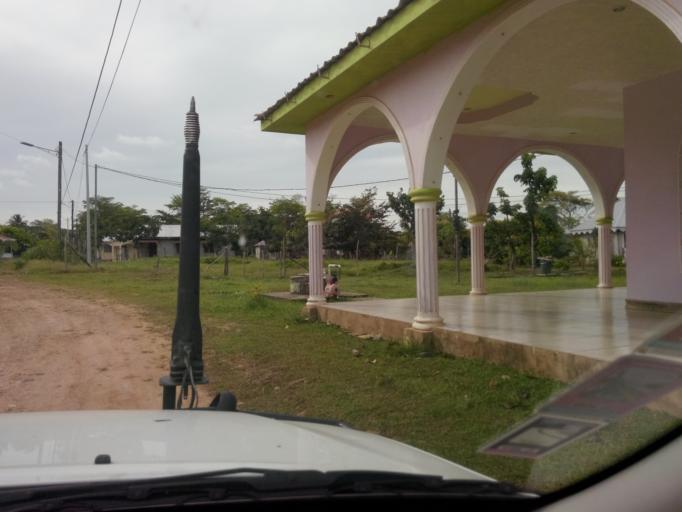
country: NI
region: Atlantico Sur
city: Bluefields
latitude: 12.0314
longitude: -83.7643
